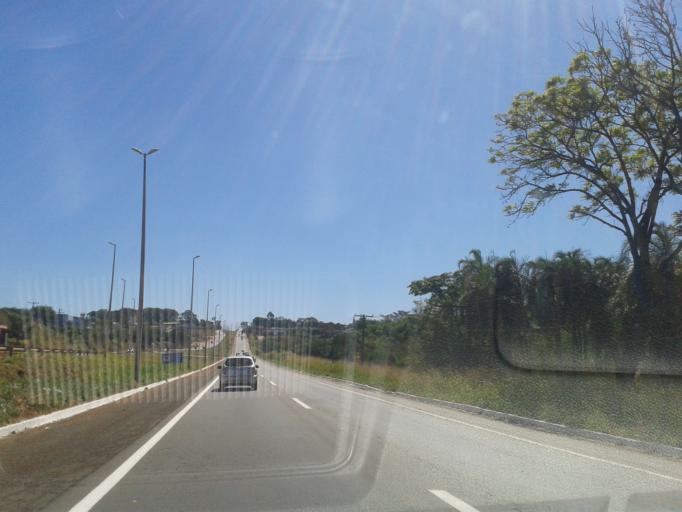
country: BR
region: Goias
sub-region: Goiania
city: Goiania
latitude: -16.6366
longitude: -49.3446
